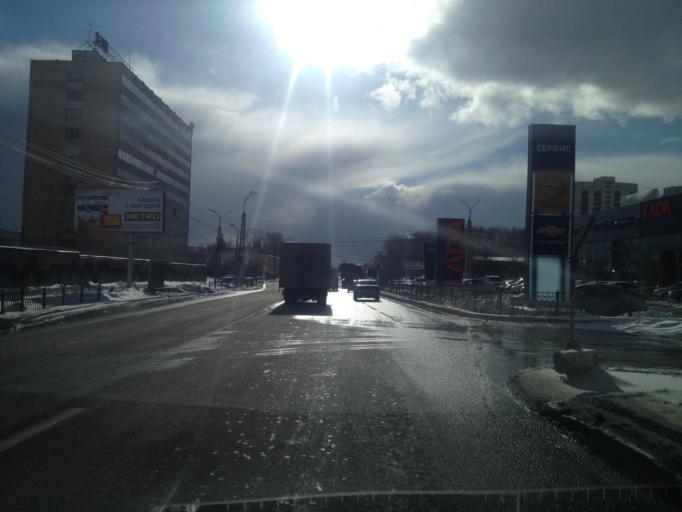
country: RU
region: Sverdlovsk
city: Yekaterinburg
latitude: 56.8841
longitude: 60.6409
